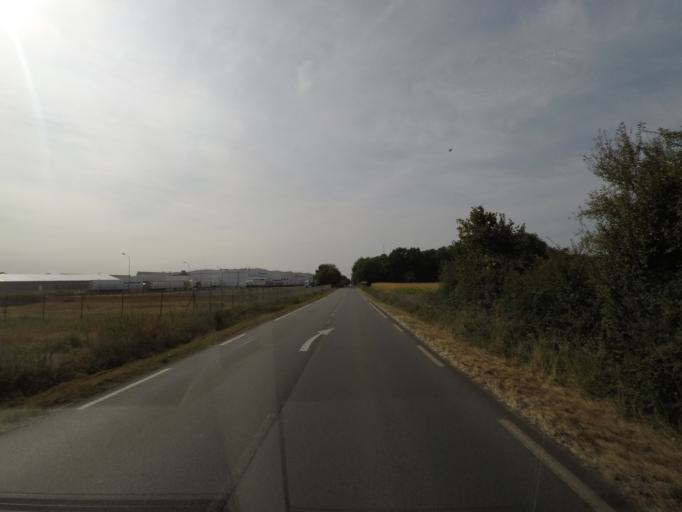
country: FR
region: Poitou-Charentes
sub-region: Departement des Deux-Sevres
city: Lezay
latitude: 46.1799
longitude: -0.0229
